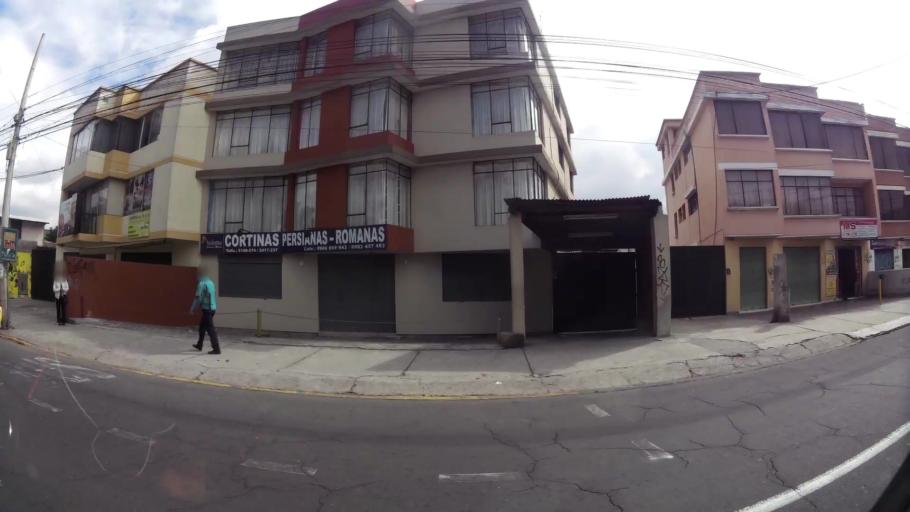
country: EC
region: Pichincha
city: Quito
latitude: -0.1541
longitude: -78.4702
